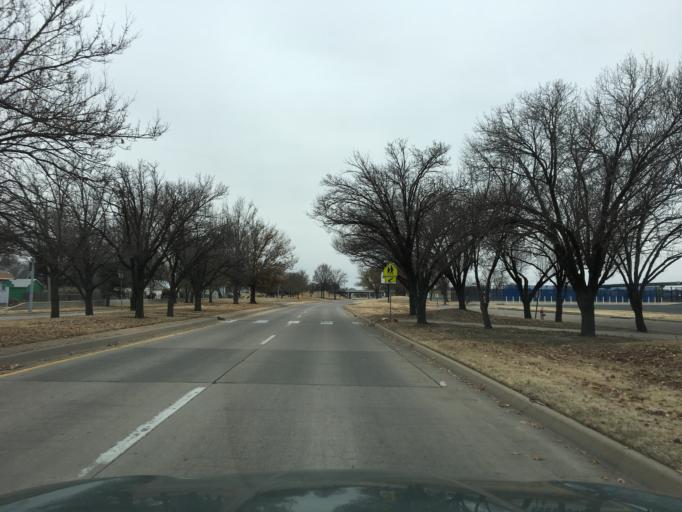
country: US
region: Kansas
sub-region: Sedgwick County
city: Wichita
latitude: 37.6832
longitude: -97.3079
